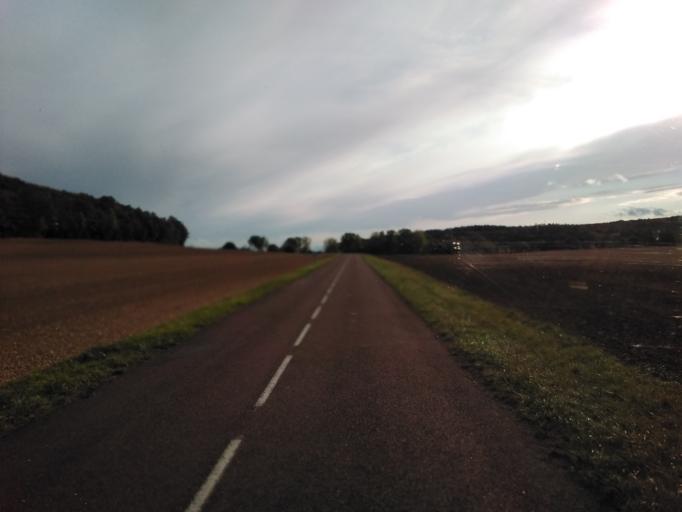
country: FR
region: Champagne-Ardenne
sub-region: Departement de l'Aube
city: Les Riceys
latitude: 47.9021
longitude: 4.3616
